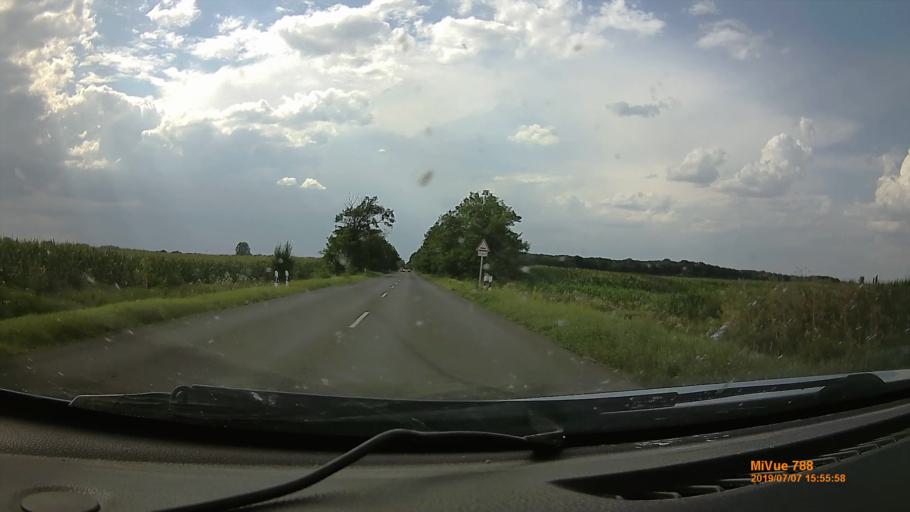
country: HU
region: Pest
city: Szentlorinckata
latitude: 47.5637
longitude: 19.7814
